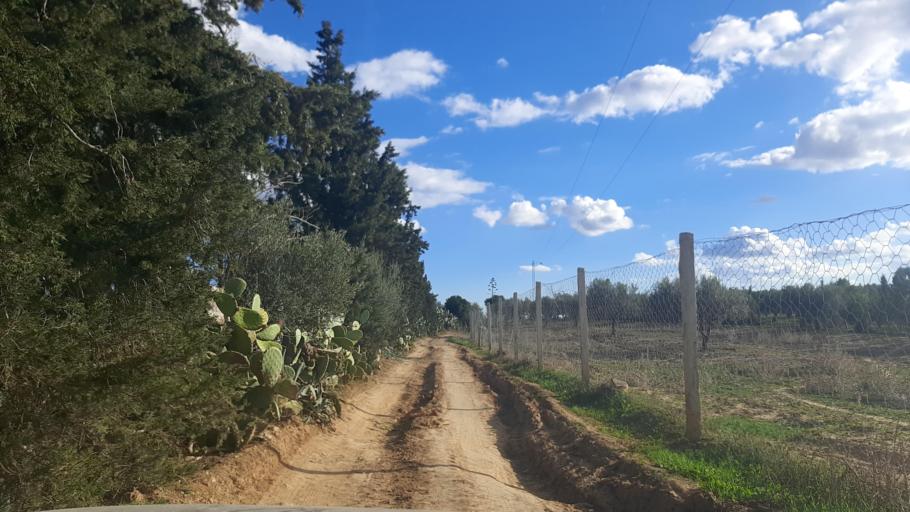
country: TN
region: Nabul
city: Bu `Urqub
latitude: 36.4518
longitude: 10.5002
